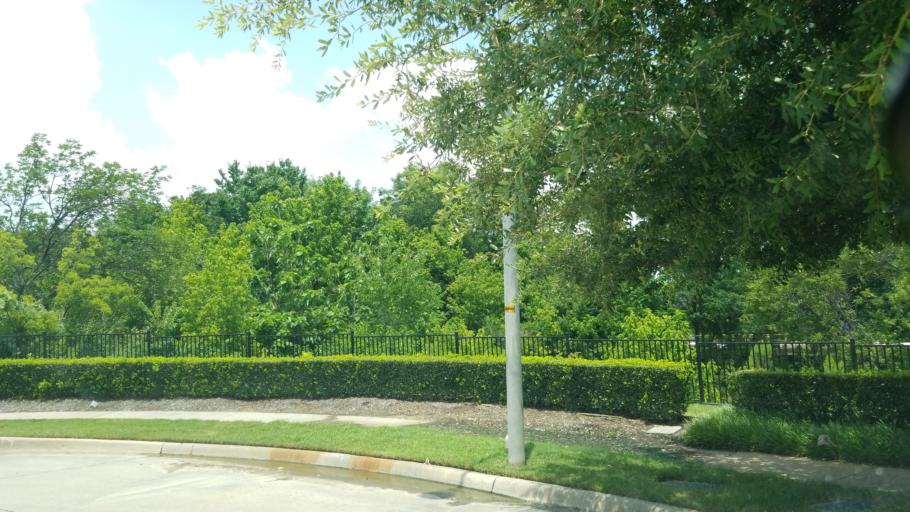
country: US
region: Texas
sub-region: Dallas County
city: Coppell
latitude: 32.9495
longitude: -96.9600
